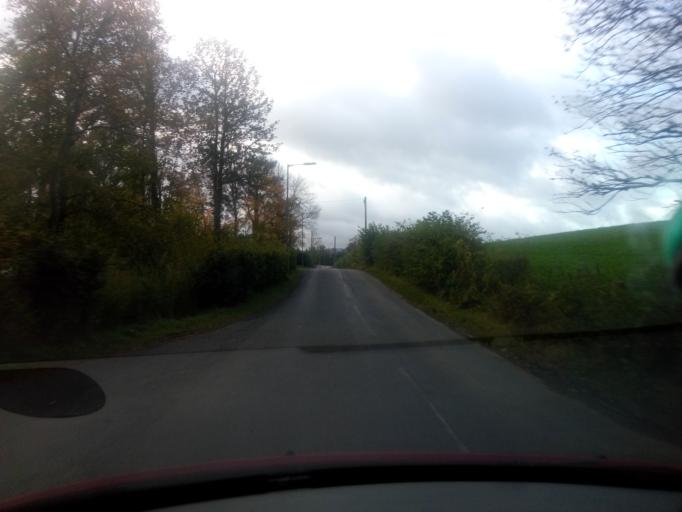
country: GB
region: Scotland
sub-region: The Scottish Borders
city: Jedburgh
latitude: 55.4050
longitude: -2.6552
